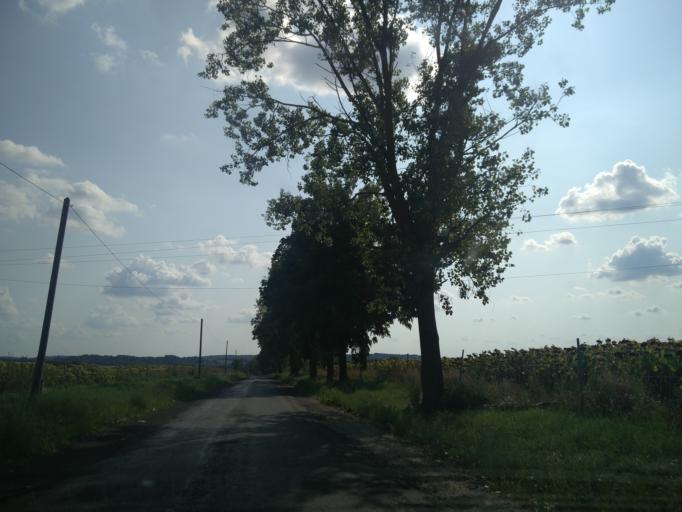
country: HU
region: Zala
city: Zalaegerszeg
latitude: 46.8903
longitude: 16.7581
